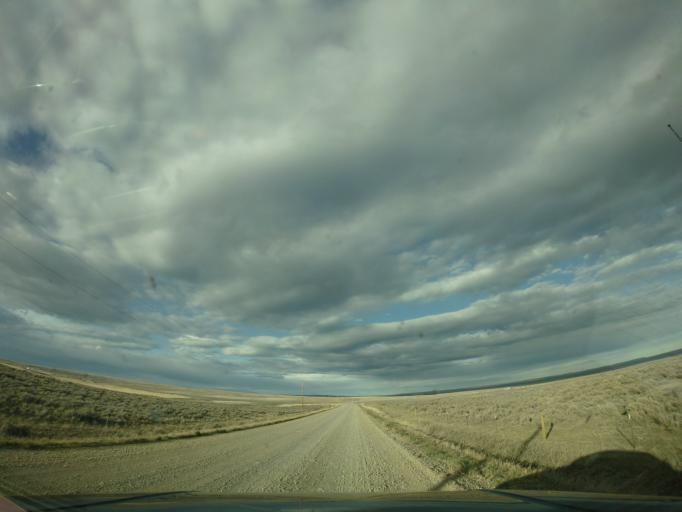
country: US
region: Montana
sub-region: Yellowstone County
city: Laurel
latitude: 45.9261
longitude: -108.8806
